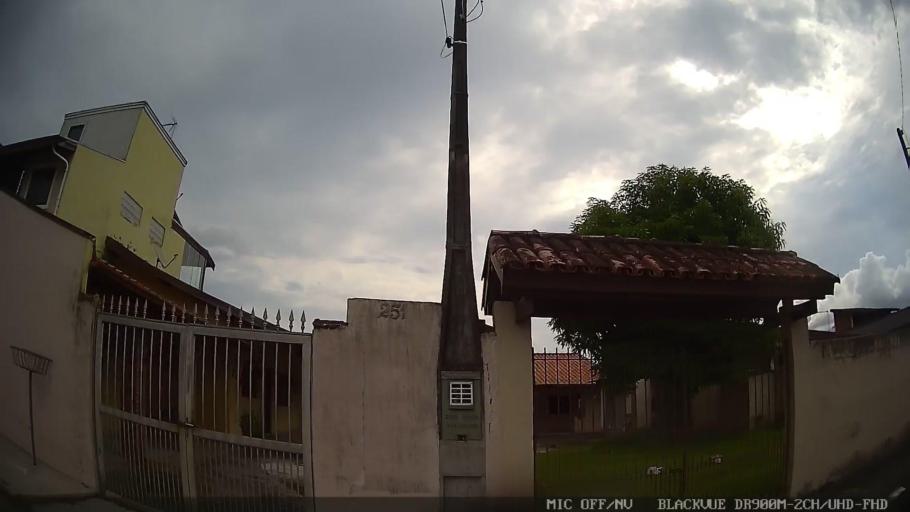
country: BR
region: Sao Paulo
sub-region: Caraguatatuba
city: Caraguatatuba
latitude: -23.6367
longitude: -45.4320
